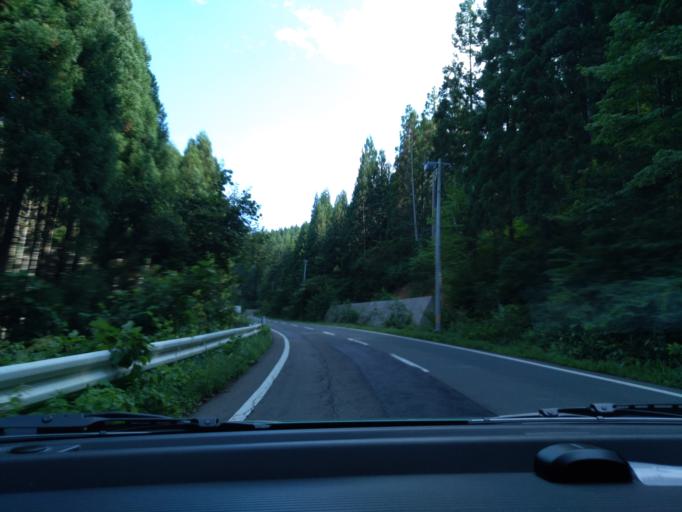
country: JP
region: Iwate
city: Shizukuishi
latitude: 39.6403
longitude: 141.0052
